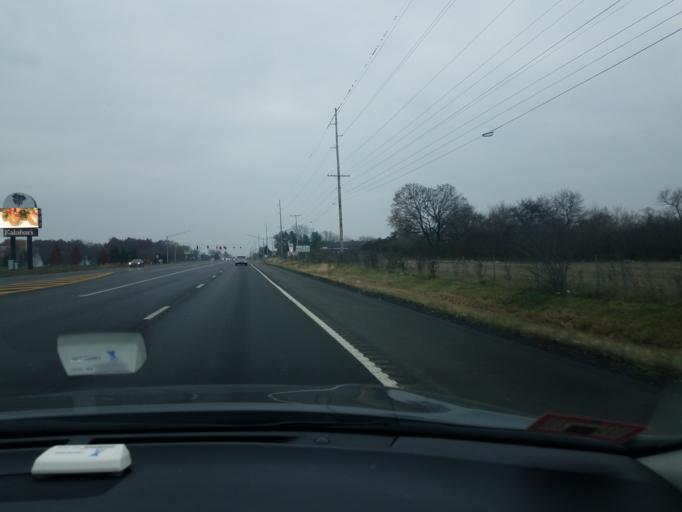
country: US
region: Ohio
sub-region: Erie County
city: Sandusky
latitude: 41.3851
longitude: -82.6471
